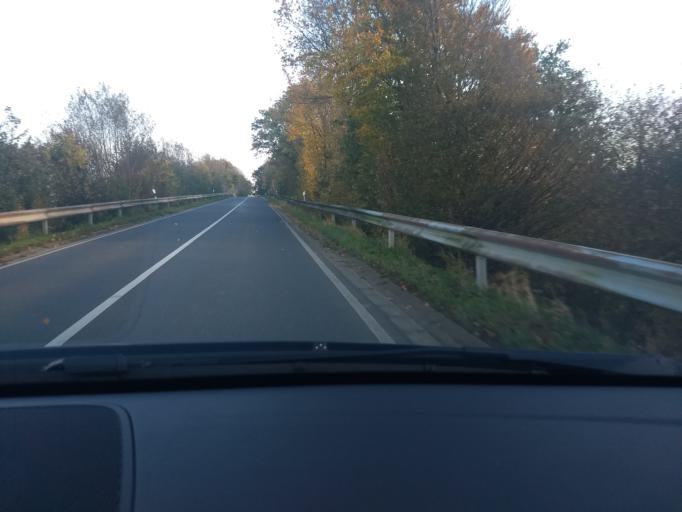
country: DE
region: North Rhine-Westphalia
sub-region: Regierungsbezirk Munster
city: Sudlohn
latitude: 51.9127
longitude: 6.8446
